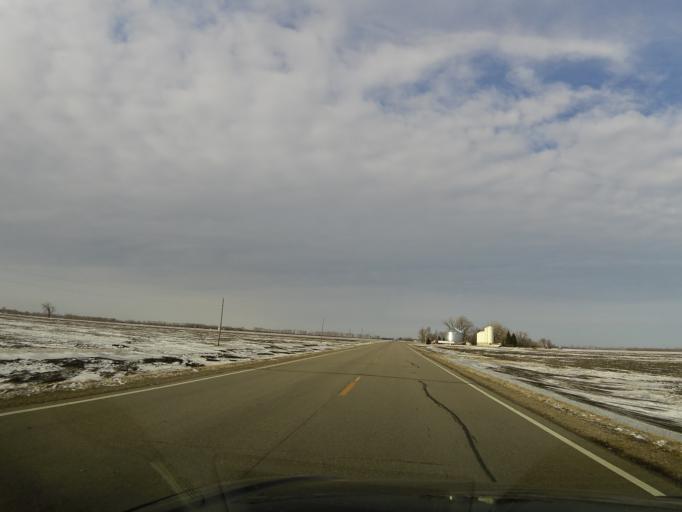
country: US
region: Minnesota
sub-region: Kittson County
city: Hallock
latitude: 48.5535
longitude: -97.1069
